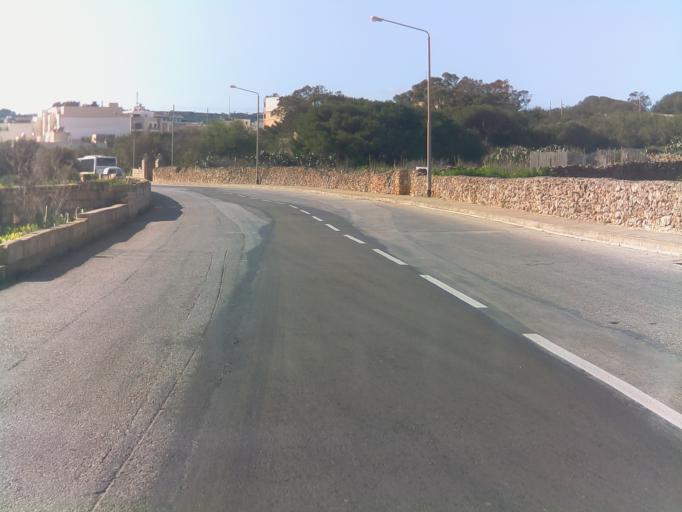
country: MT
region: L-Imgarr
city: Imgarr
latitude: 35.9254
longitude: 14.3678
